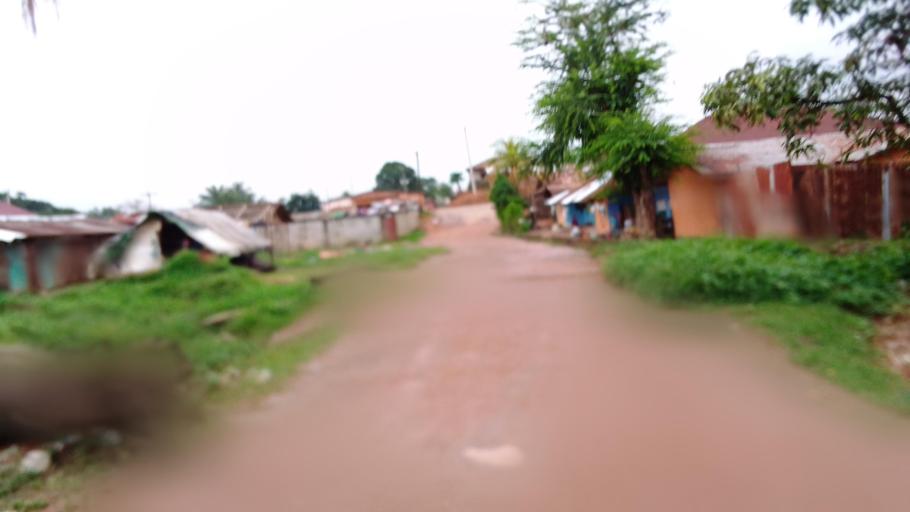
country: SL
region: Eastern Province
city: Kenema
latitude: 7.8702
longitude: -11.1912
